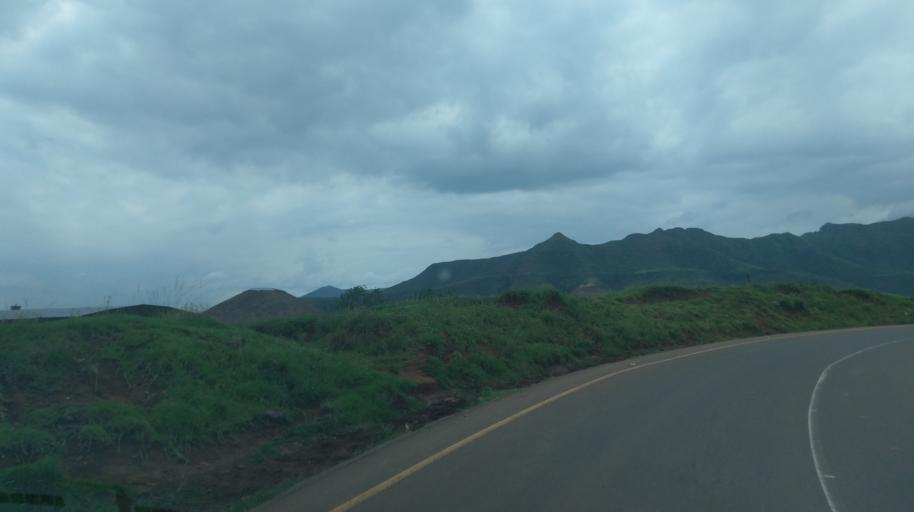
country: LS
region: Butha-Buthe
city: Butha-Buthe
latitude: -29.0332
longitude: 28.2656
